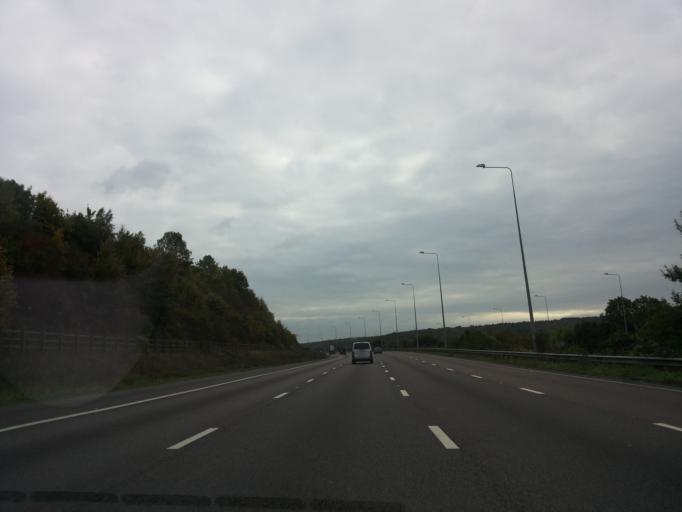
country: GB
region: England
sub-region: Medway
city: Rochester
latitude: 51.3639
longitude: 0.4899
